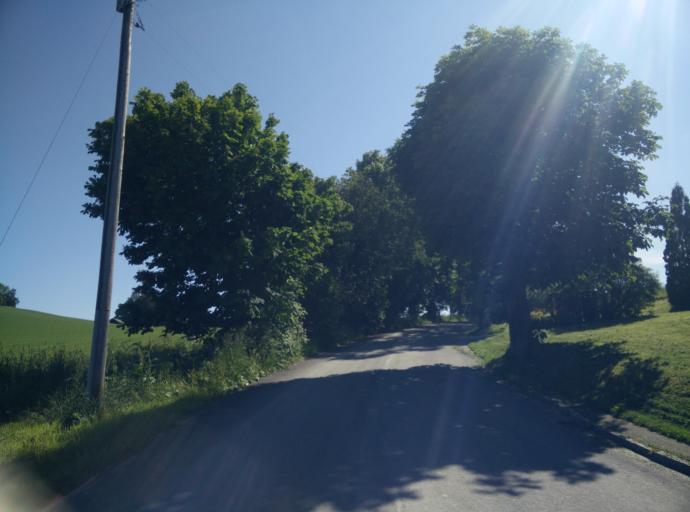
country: NO
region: Sor-Trondelag
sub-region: Trondheim
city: Trondheim
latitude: 63.4091
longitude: 10.3733
